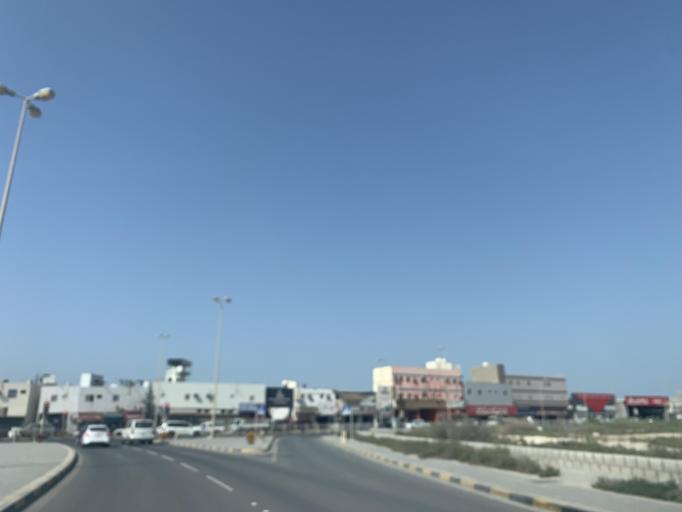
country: BH
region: Central Governorate
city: Madinat Hamad
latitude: 26.1389
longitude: 50.4888
